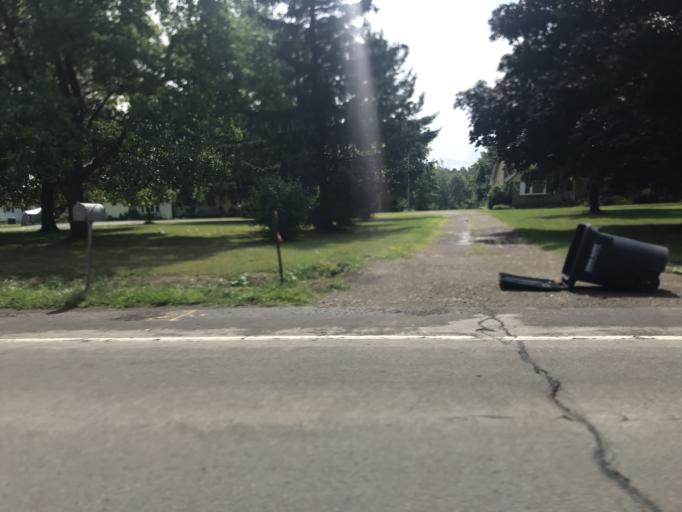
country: US
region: New York
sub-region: Chautauqua County
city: Dunkirk
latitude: 42.5086
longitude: -79.2848
